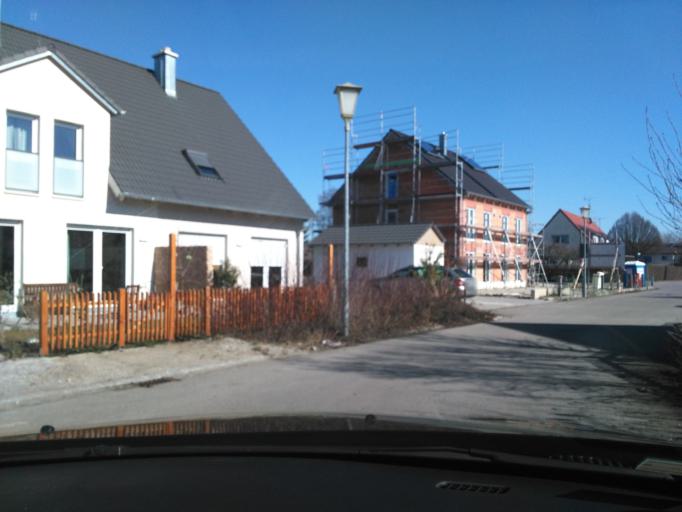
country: DE
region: Bavaria
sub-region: Upper Bavaria
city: Mammendorf
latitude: 48.2150
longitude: 11.1728
